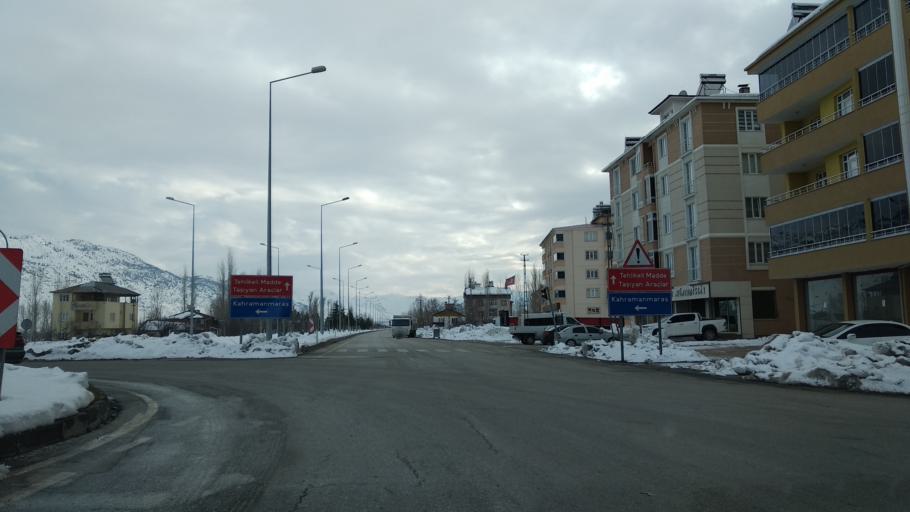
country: TR
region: Kahramanmaras
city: Goksun
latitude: 38.0141
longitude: 36.5025
